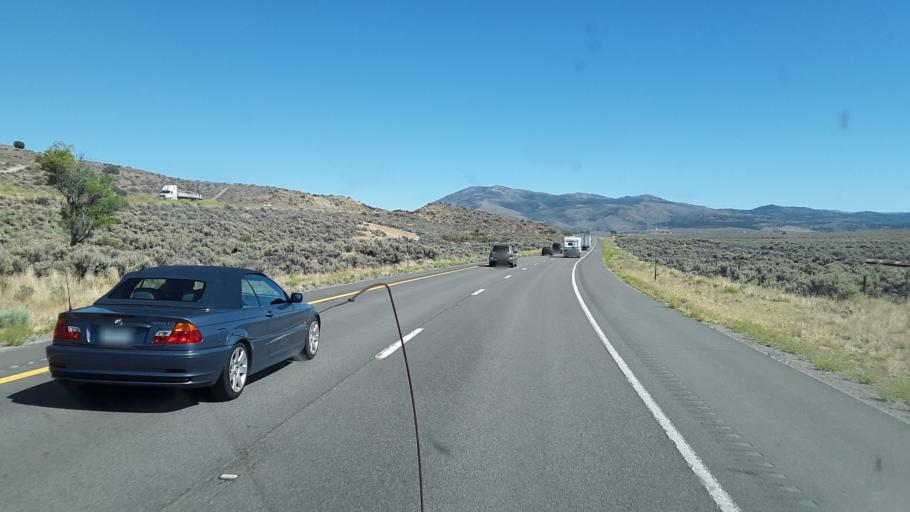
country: US
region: Nevada
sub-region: Washoe County
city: Cold Springs
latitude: 39.6889
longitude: -120.0146
